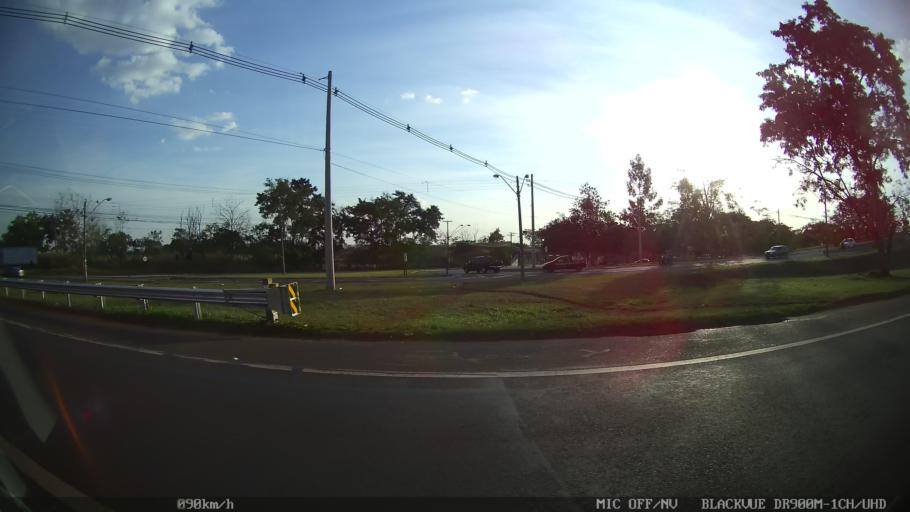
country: BR
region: Sao Paulo
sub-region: Ribeirao Preto
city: Ribeirao Preto
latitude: -21.1224
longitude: -47.7863
